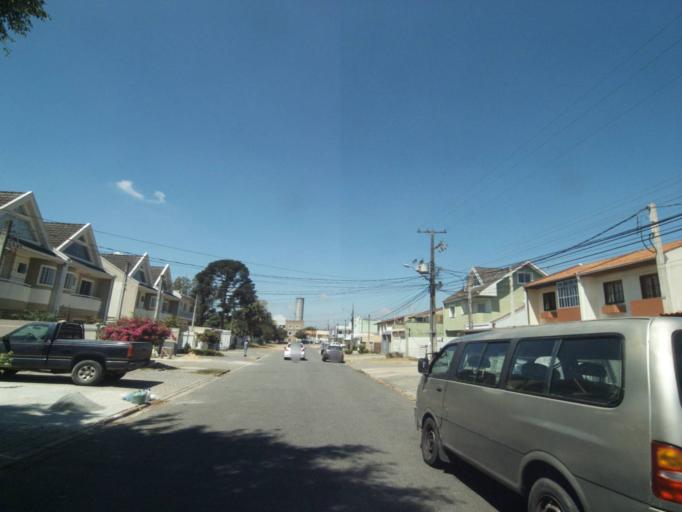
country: BR
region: Parana
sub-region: Sao Jose Dos Pinhais
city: Sao Jose dos Pinhais
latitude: -25.5125
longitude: -49.2418
